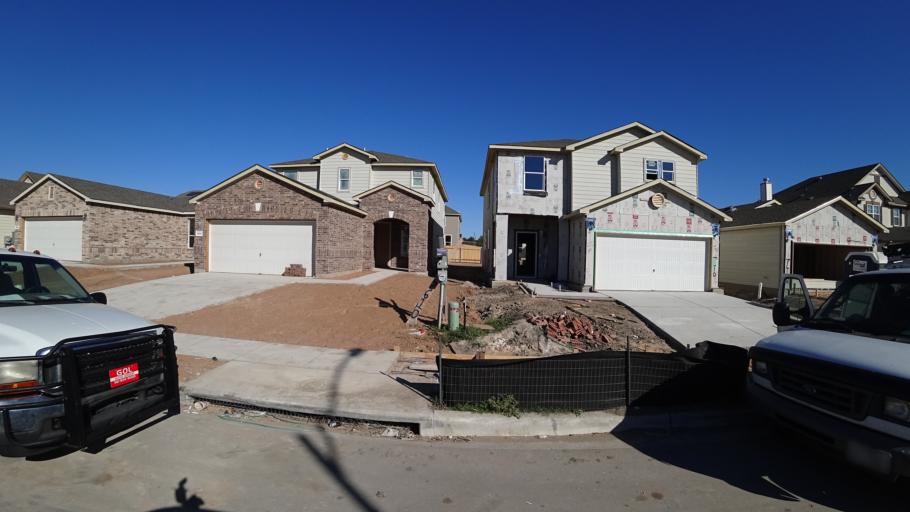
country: US
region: Texas
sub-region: Travis County
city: Hornsby Bend
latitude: 30.3164
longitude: -97.6546
